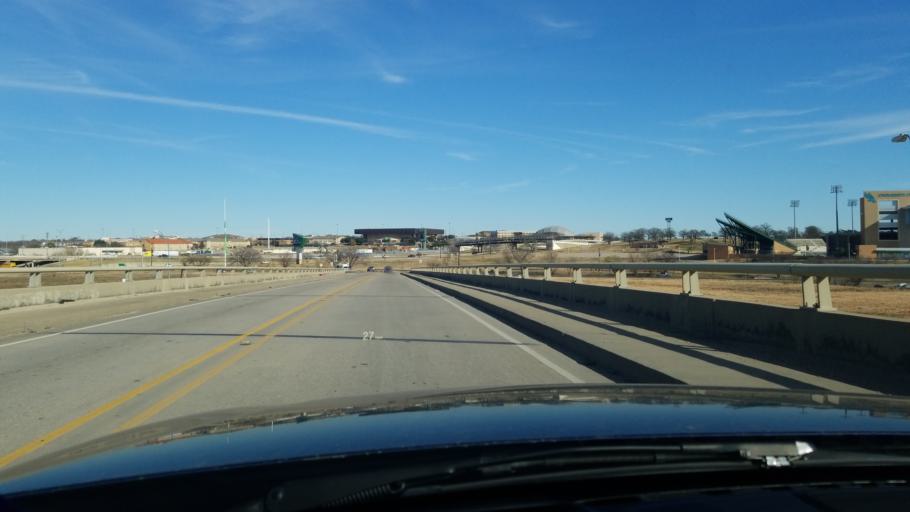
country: US
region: Texas
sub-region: Denton County
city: Denton
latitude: 33.2053
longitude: -97.1646
